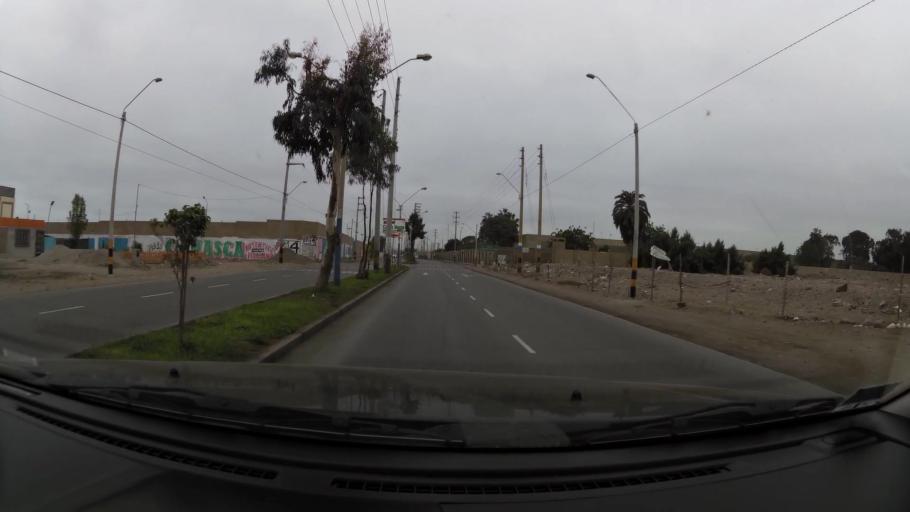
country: PE
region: Ica
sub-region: Provincia de Pisco
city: Pisco
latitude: -13.7144
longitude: -76.1945
